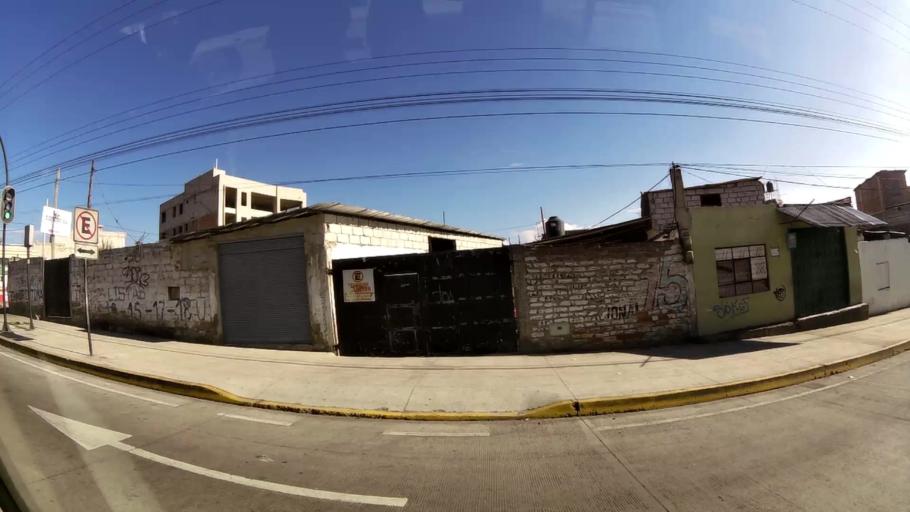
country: EC
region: Chimborazo
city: Riobamba
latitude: -1.6587
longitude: -78.6863
